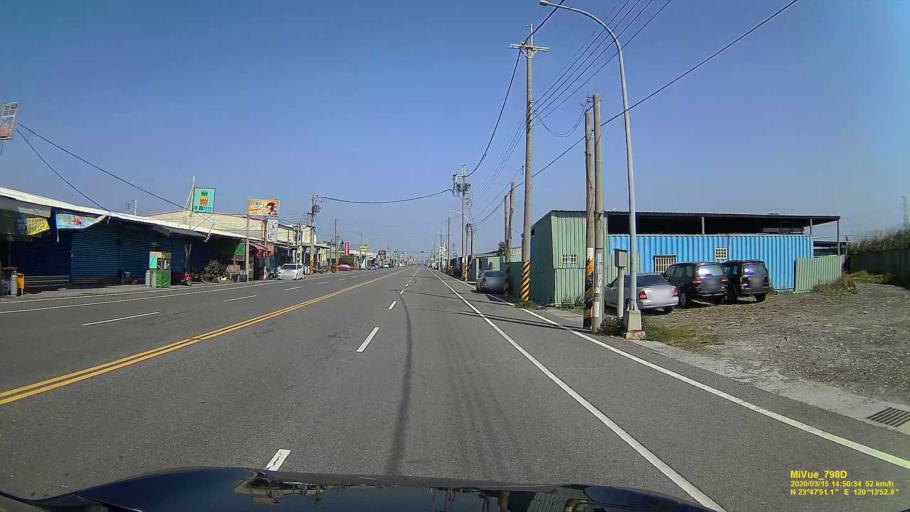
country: TW
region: Taiwan
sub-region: Yunlin
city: Douliu
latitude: 23.7977
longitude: 120.2316
